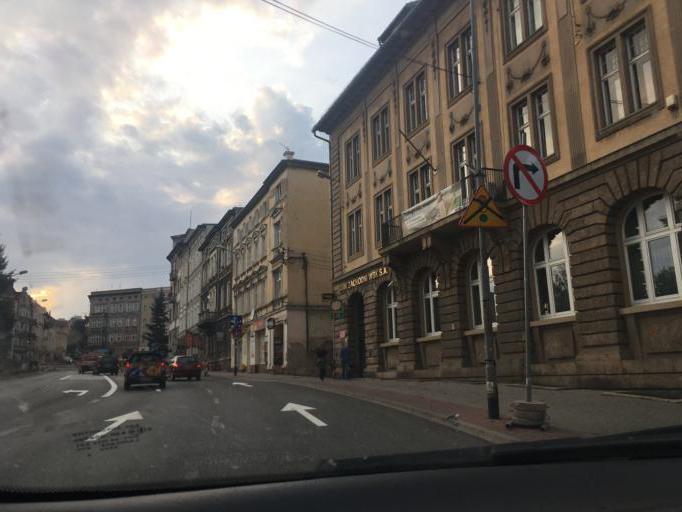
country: PL
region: Lower Silesian Voivodeship
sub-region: Powiat klodzki
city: Klodzko
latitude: 50.4358
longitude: 16.6522
